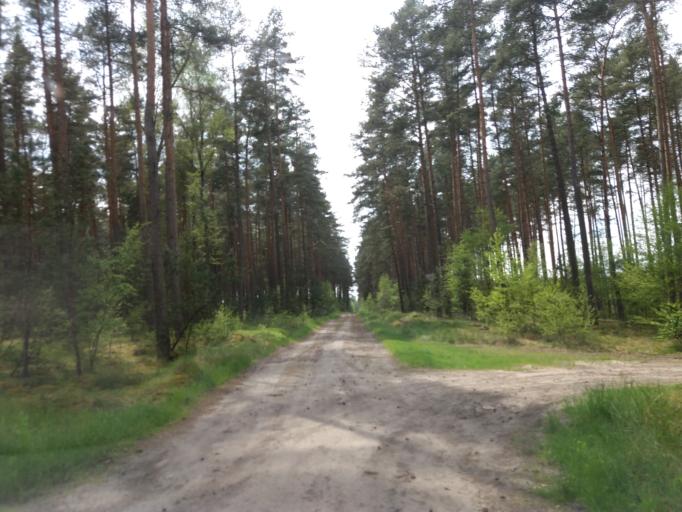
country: PL
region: West Pomeranian Voivodeship
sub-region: Powiat choszczenski
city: Drawno
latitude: 53.1937
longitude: 15.7454
